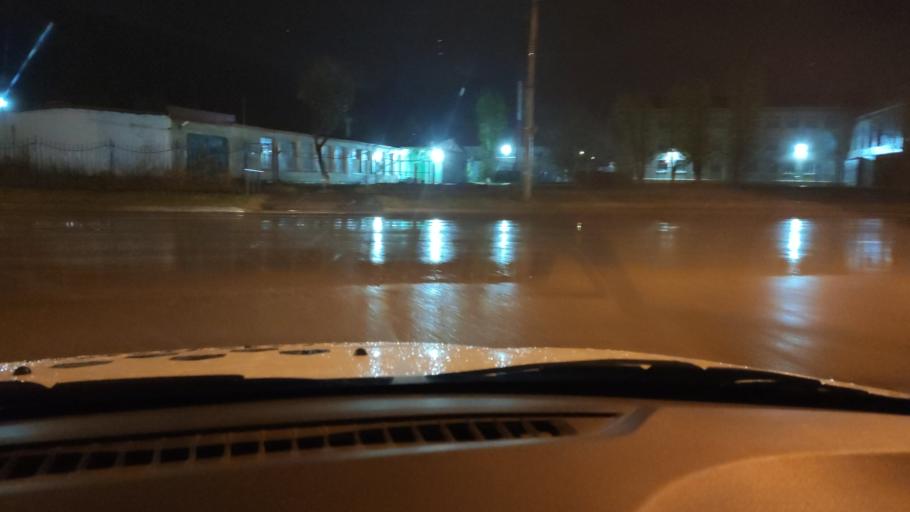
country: RU
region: Perm
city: Perm
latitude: 57.9753
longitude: 56.2432
